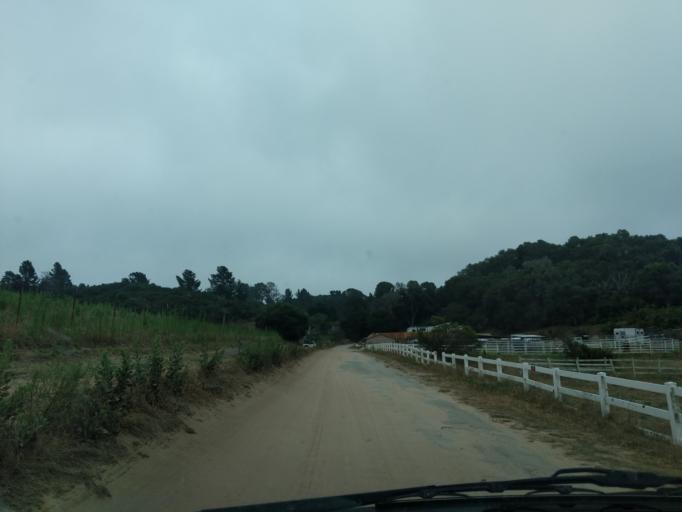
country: US
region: California
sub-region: Monterey County
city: Prunedale
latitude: 36.8109
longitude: -121.6426
